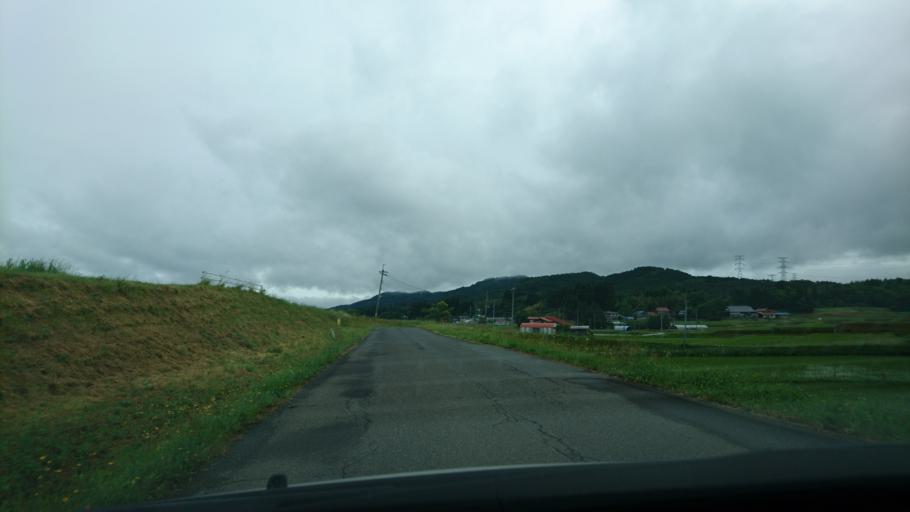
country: JP
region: Iwate
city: Ichinoseki
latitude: 38.9154
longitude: 141.2055
